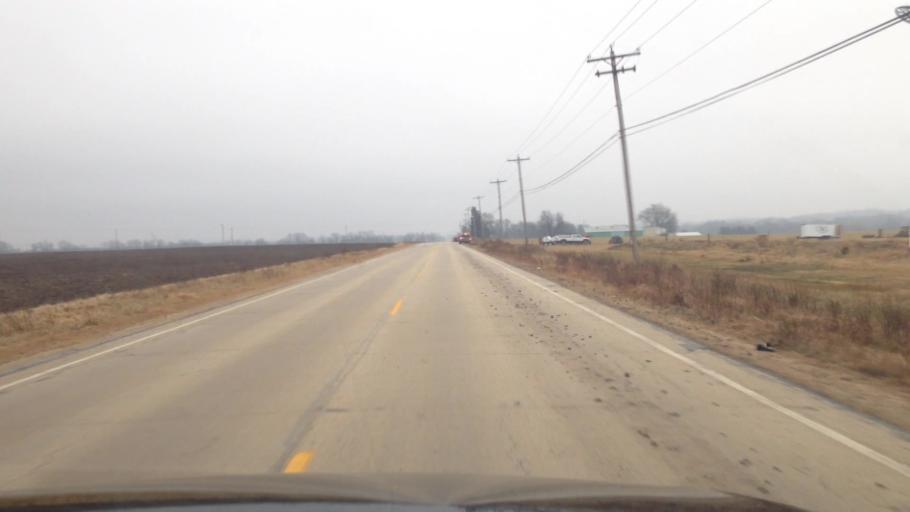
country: US
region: Wisconsin
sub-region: Washington County
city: Richfield
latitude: 43.2549
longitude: -88.1626
